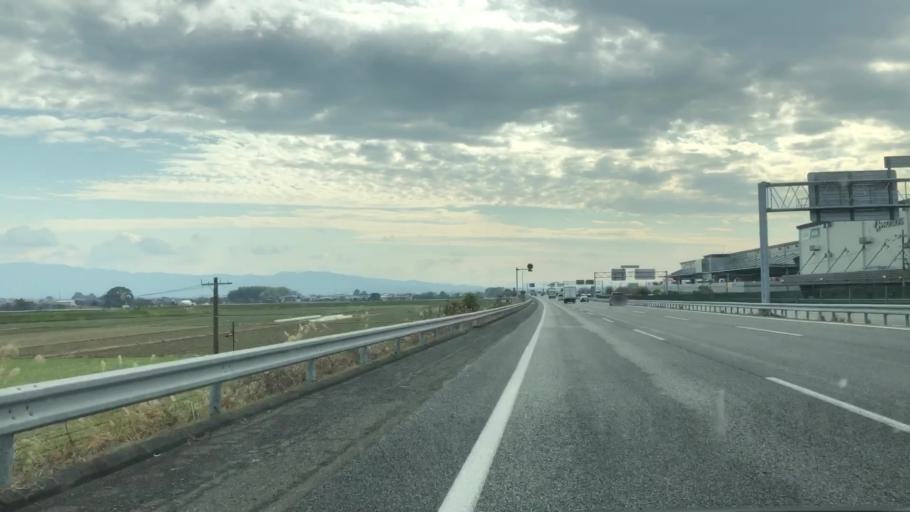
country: JP
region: Saga Prefecture
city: Tosu
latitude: 33.3909
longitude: 130.5384
